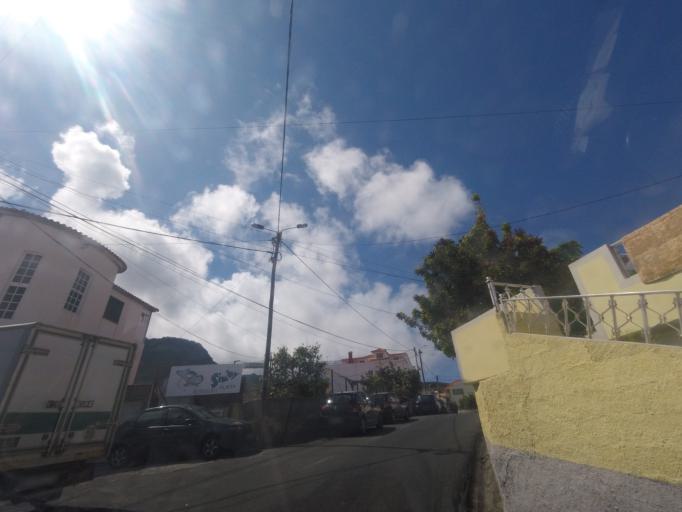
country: PT
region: Madeira
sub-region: Machico
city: Canical
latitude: 32.7393
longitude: -16.7384
